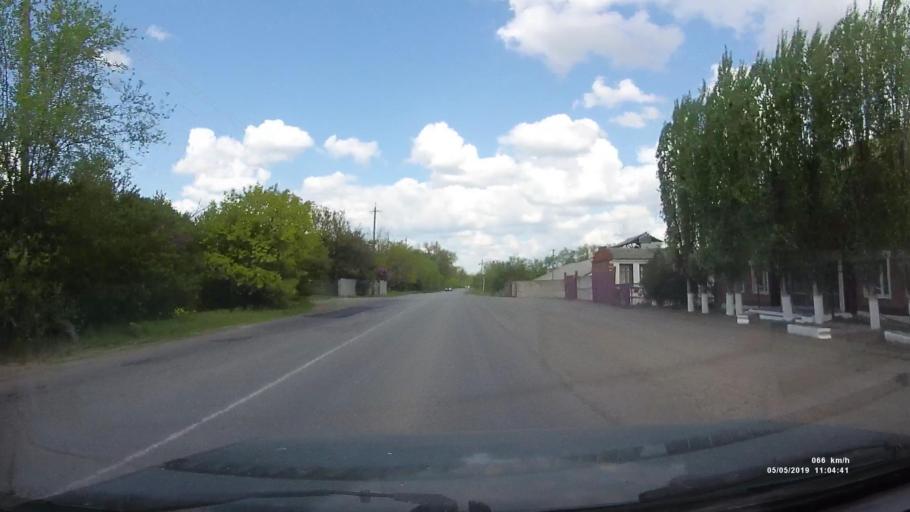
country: RU
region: Rostov
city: Ust'-Donetskiy
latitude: 47.6993
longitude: 40.9157
